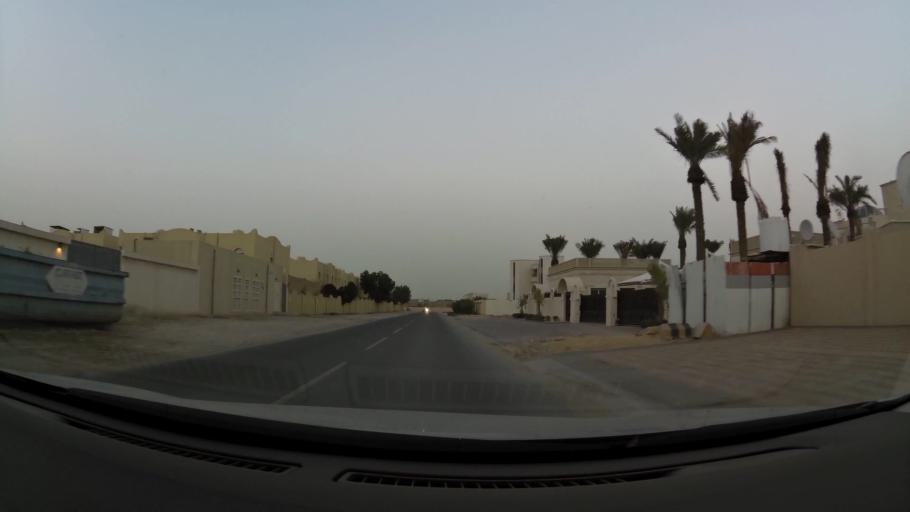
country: QA
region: Baladiyat ar Rayyan
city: Ar Rayyan
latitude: 25.2543
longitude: 51.4646
